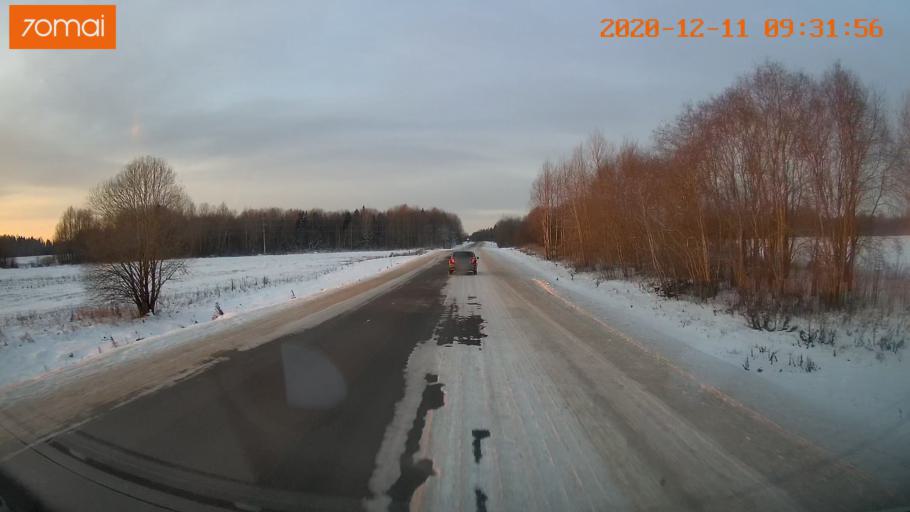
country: RU
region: Vologda
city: Vologda
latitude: 59.1256
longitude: 39.9762
